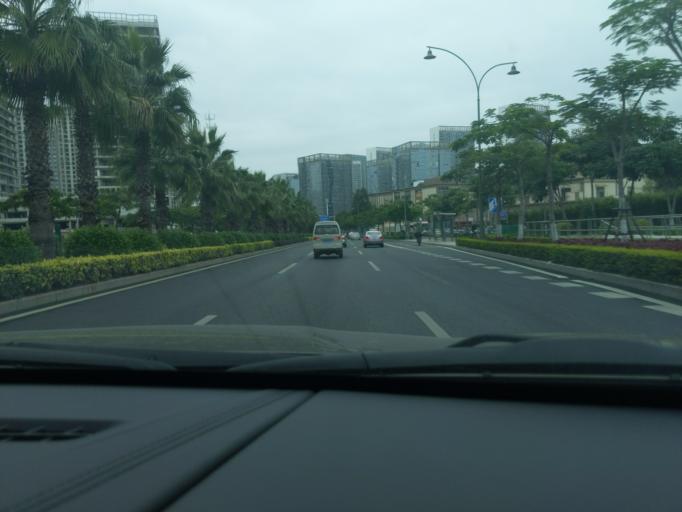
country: CN
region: Fujian
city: Liuwudian
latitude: 24.5010
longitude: 118.1717
